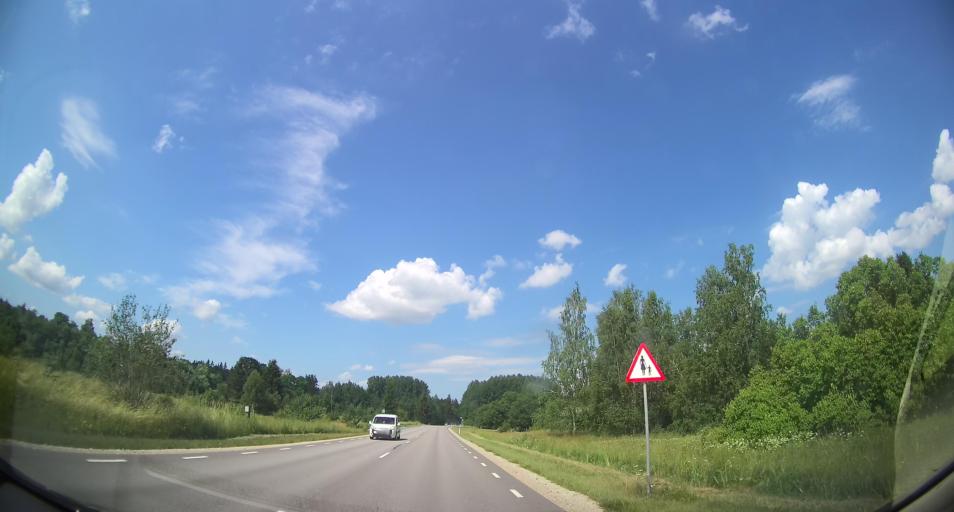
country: EE
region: Raplamaa
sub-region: Maerjamaa vald
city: Marjamaa
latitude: 58.9239
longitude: 24.4007
